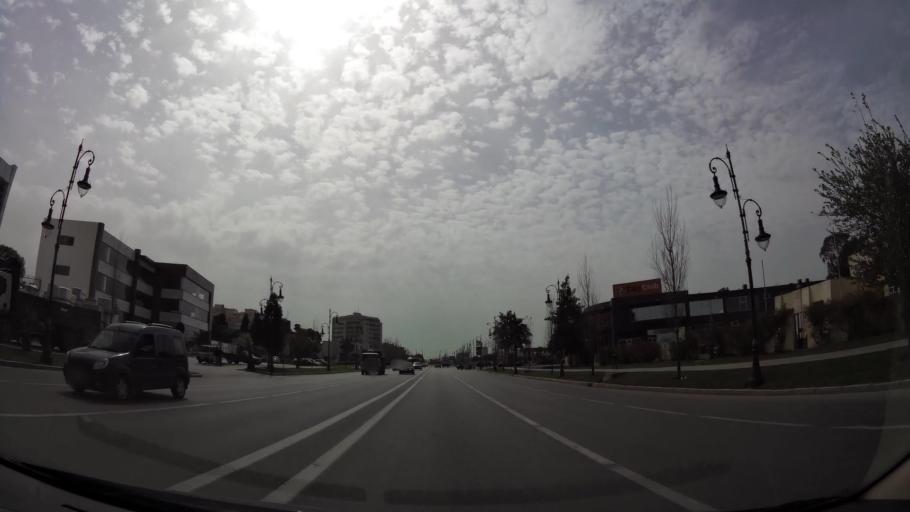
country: MA
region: Tanger-Tetouan
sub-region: Tanger-Assilah
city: Boukhalef
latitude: 35.7390
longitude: -5.8503
